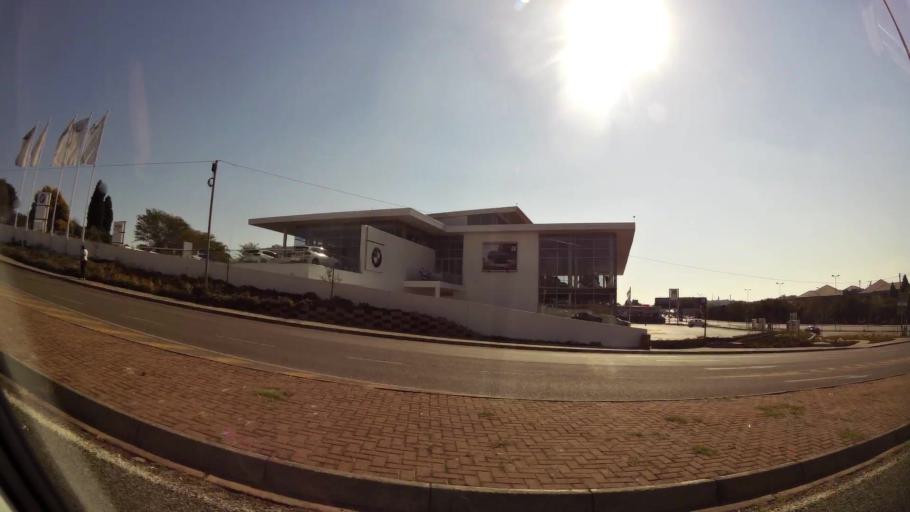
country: ZA
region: Gauteng
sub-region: City of Tshwane Metropolitan Municipality
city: Pretoria
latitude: -25.7888
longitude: 28.2747
